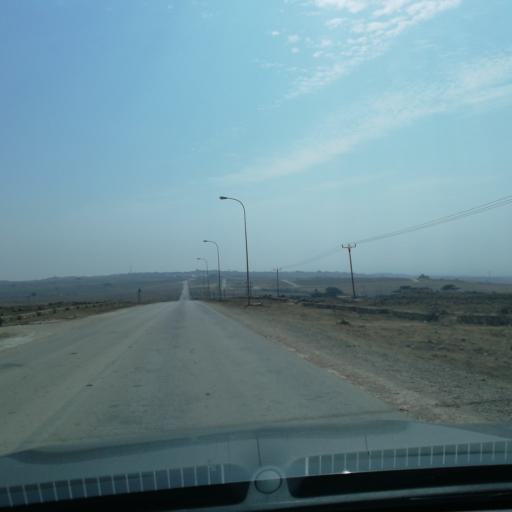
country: OM
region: Zufar
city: Salalah
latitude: 17.2394
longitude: 54.0565
